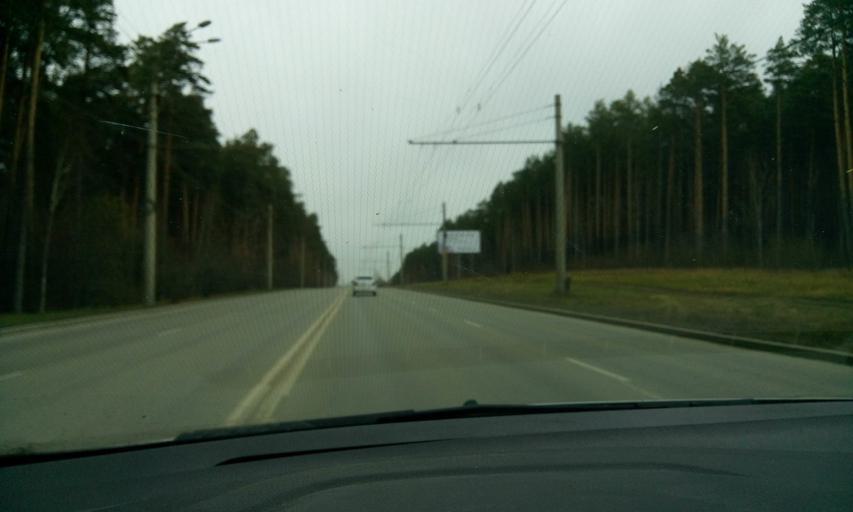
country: RU
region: Sverdlovsk
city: Sovkhoznyy
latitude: 56.7852
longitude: 60.5651
